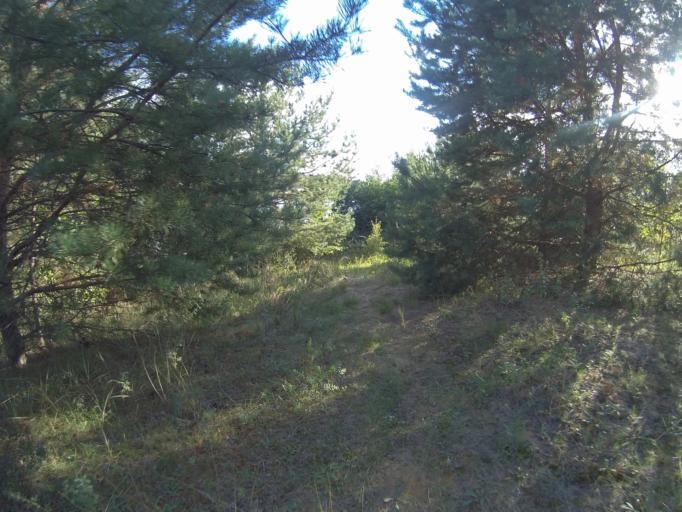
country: RU
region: Vladimir
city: Kommunar
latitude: 56.0413
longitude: 40.4246
